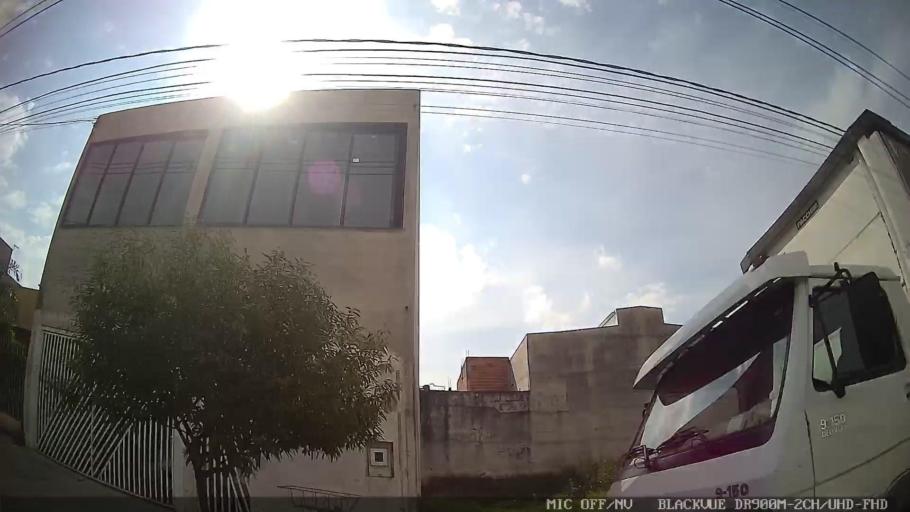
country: BR
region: Sao Paulo
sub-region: Indaiatuba
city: Indaiatuba
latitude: -23.1255
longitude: -47.2514
